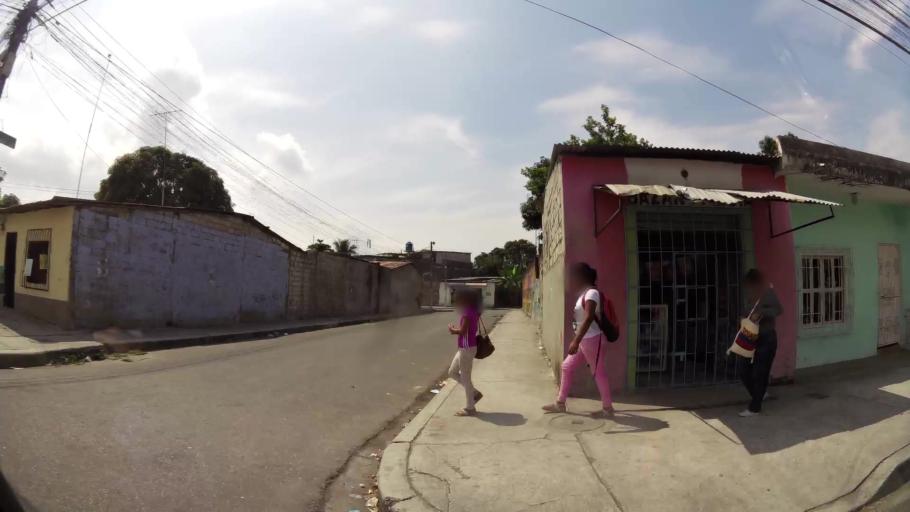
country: EC
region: Guayas
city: Guayaquil
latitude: -2.2630
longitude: -79.8745
